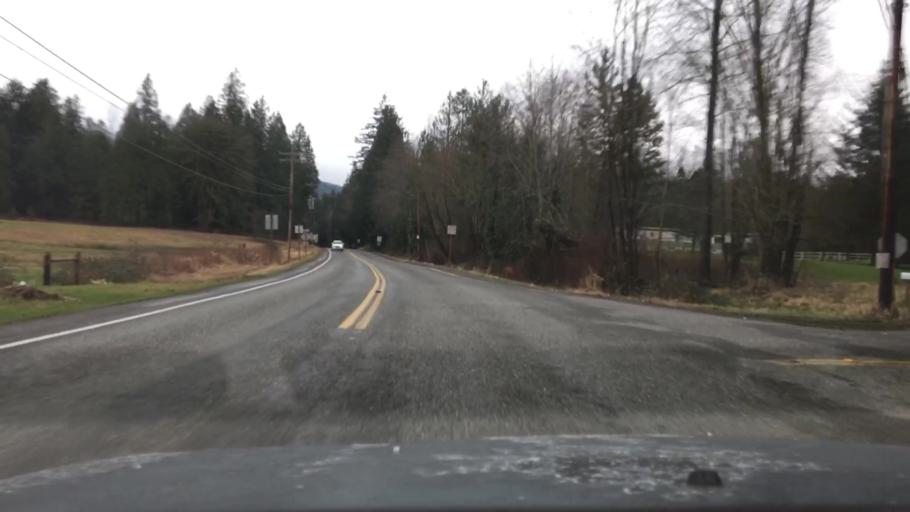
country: US
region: Washington
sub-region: Whatcom County
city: Sudden Valley
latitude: 48.6465
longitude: -122.3241
